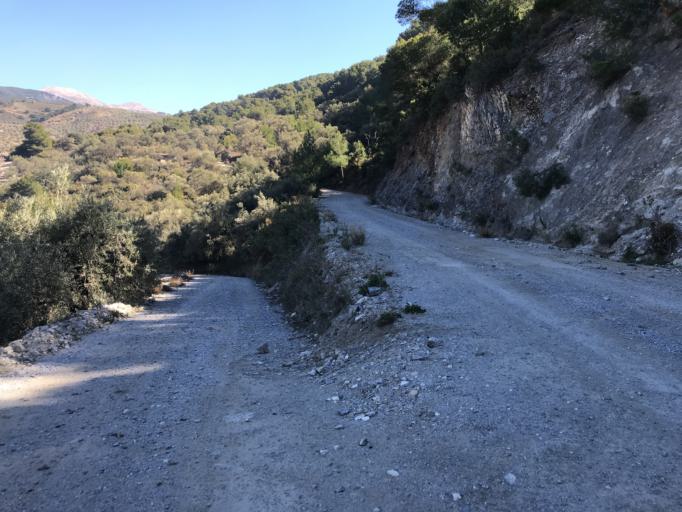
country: ES
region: Andalusia
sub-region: Provincia de Malaga
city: Canillas de Albaida
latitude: 36.8586
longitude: -3.9876
